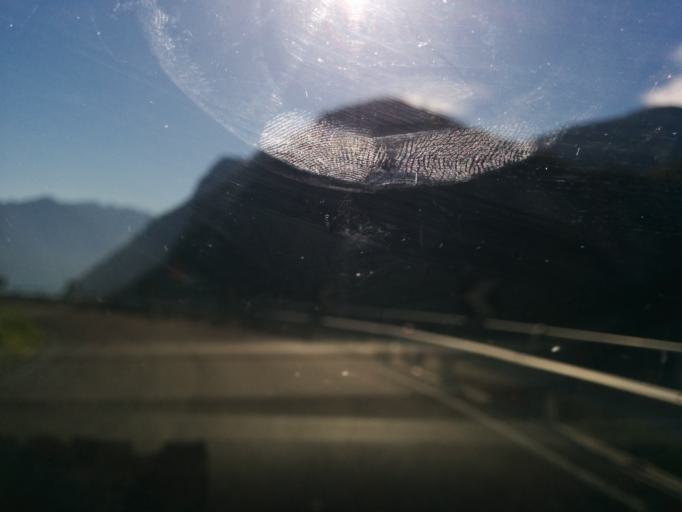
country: IT
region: Trentino-Alto Adige
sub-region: Provincia di Trento
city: Tenno
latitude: 45.9222
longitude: 10.8304
